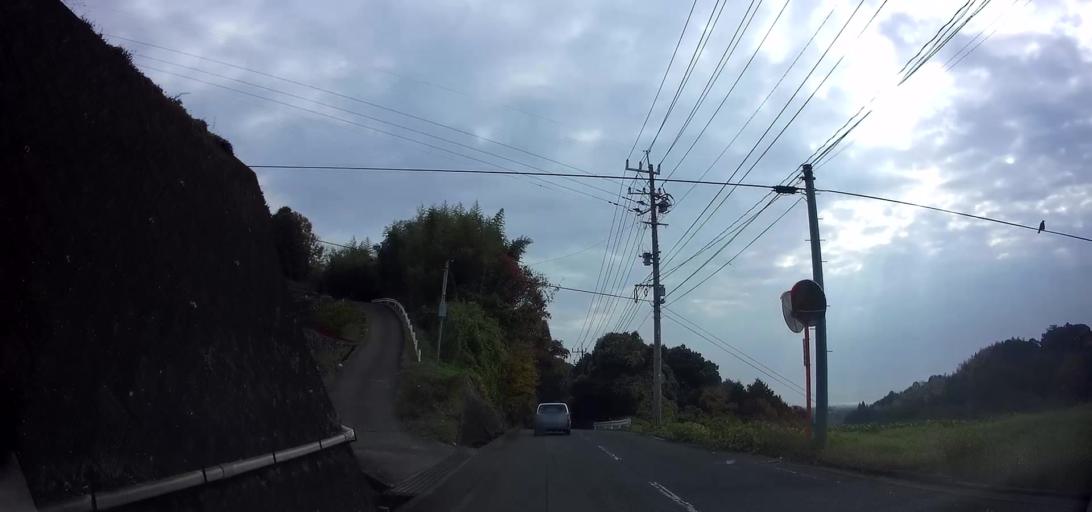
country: JP
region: Nagasaki
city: Shimabara
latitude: 32.6875
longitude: 130.2864
